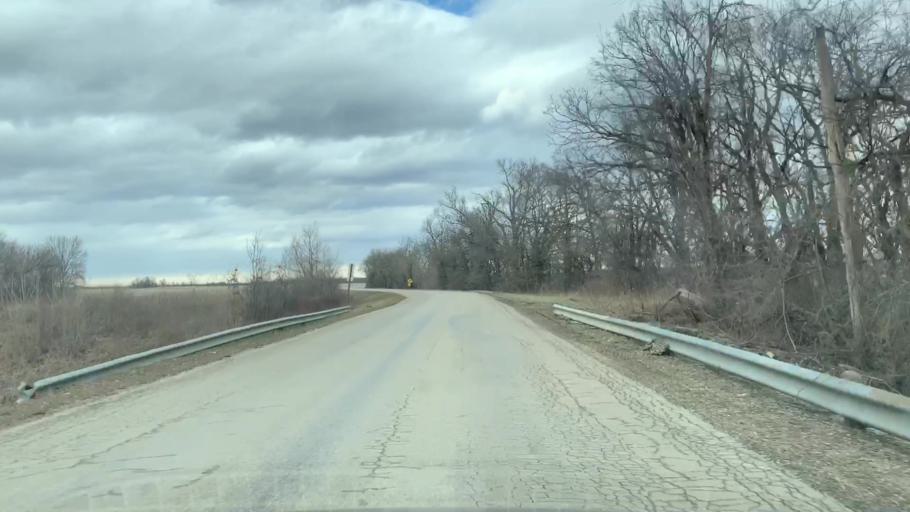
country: US
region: Kansas
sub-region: Allen County
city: Humboldt
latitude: 37.8098
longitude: -95.4707
